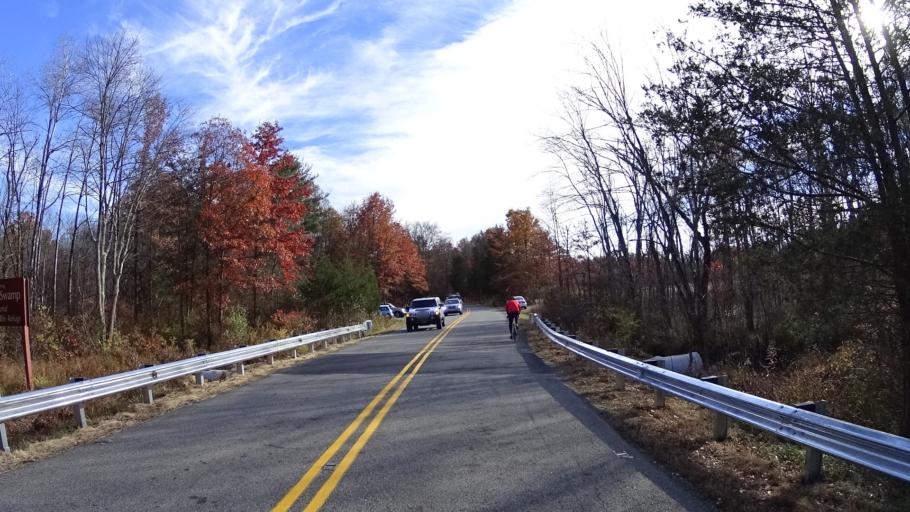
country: US
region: New Jersey
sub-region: Union County
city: Berkeley Heights
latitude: 40.7278
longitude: -74.4952
